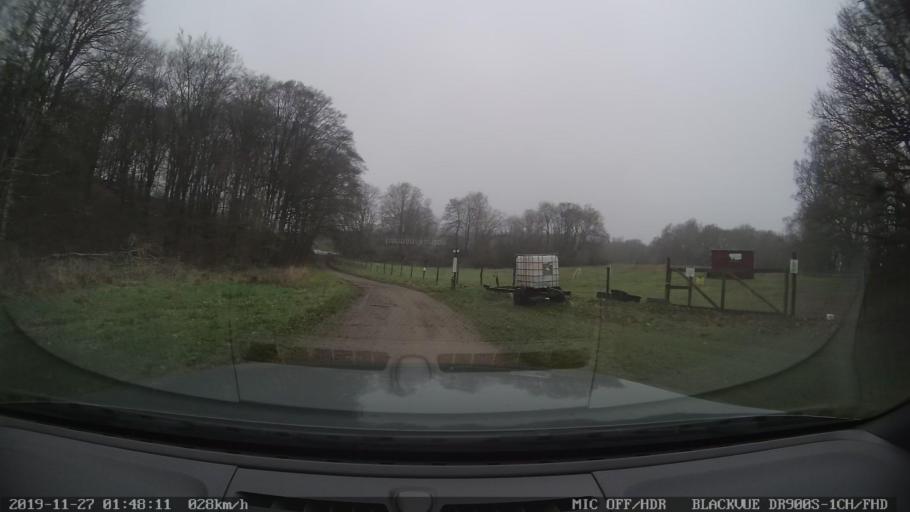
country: SE
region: Skane
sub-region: Hoganas Kommun
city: Hoganas
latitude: 56.2788
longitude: 12.5464
